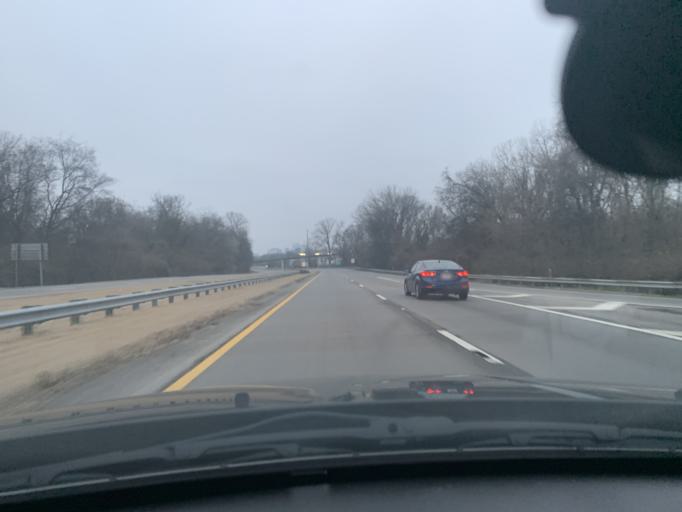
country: US
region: Tennessee
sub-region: Davidson County
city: Nashville
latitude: 36.1834
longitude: -86.7611
